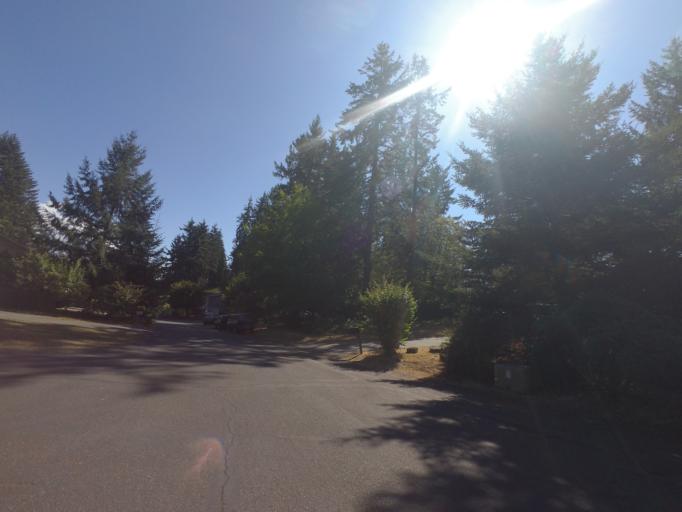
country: US
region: Washington
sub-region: Pierce County
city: Fircrest
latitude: 47.2167
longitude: -122.5203
